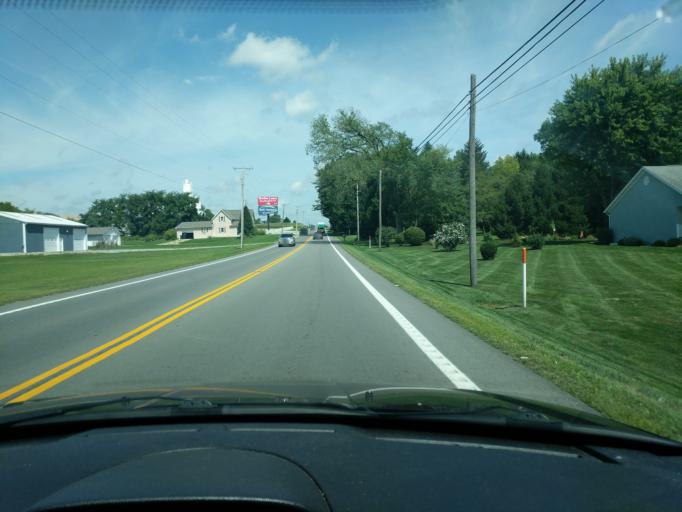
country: US
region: Ohio
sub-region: Logan County
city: West Liberty
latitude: 40.3026
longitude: -83.7593
